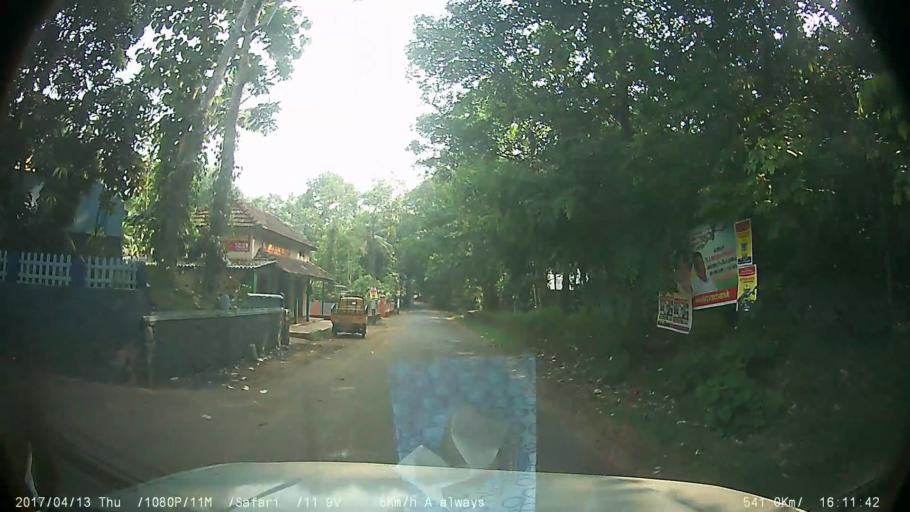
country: IN
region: Kerala
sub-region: Ernakulam
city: Piravam
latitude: 9.8211
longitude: 76.5203
